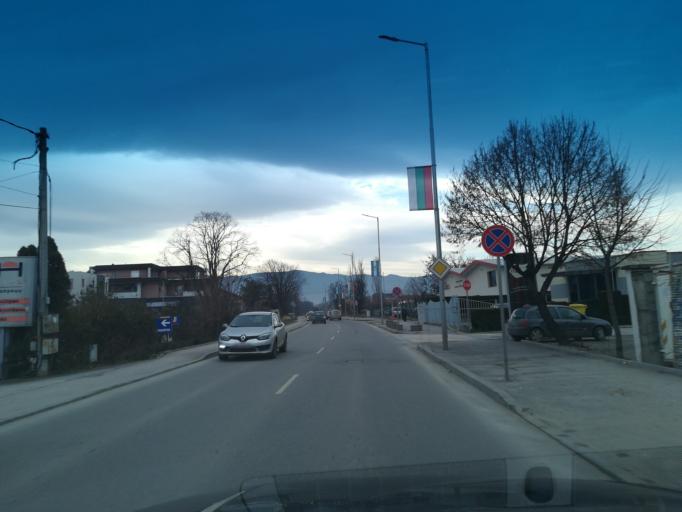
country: BG
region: Plovdiv
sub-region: Obshtina Plovdiv
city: Plovdiv
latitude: 42.1165
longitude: 24.7130
